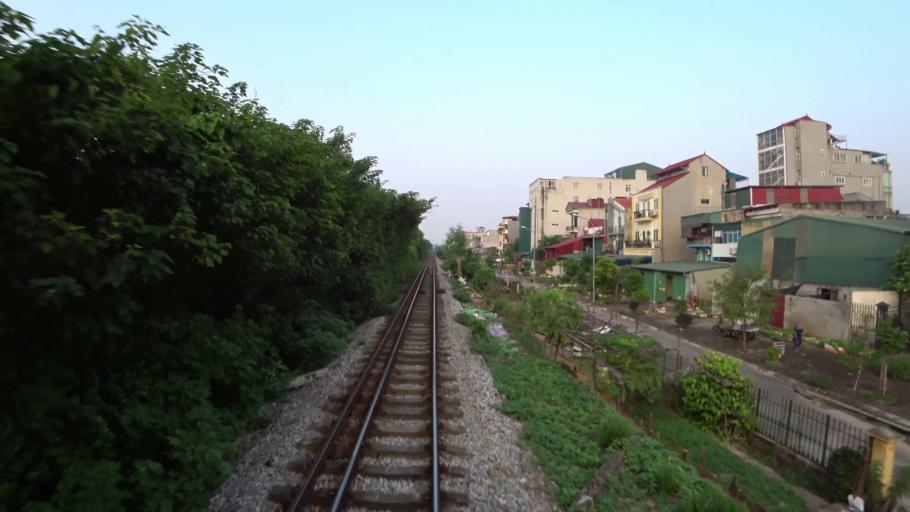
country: VN
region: Ha Noi
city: Trau Quy
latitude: 21.0827
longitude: 105.9134
